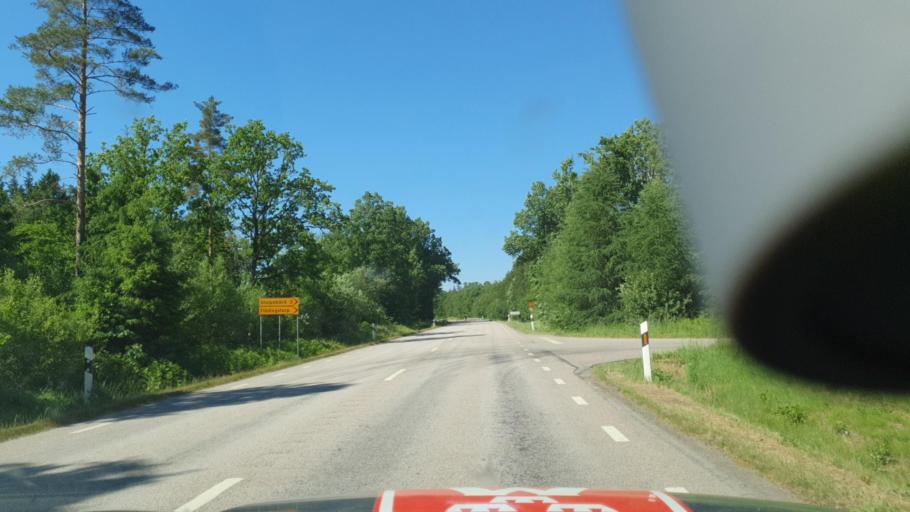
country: SE
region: Kalmar
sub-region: Emmaboda Kommun
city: Emmaboda
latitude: 56.5458
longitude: 15.6119
